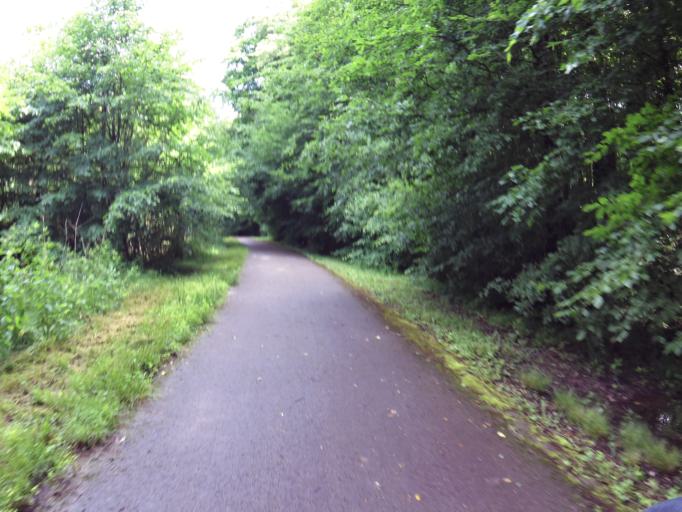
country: FR
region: Champagne-Ardenne
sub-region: Departement de l'Aube
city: Lusigny-sur-Barse
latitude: 48.2896
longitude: 4.3049
